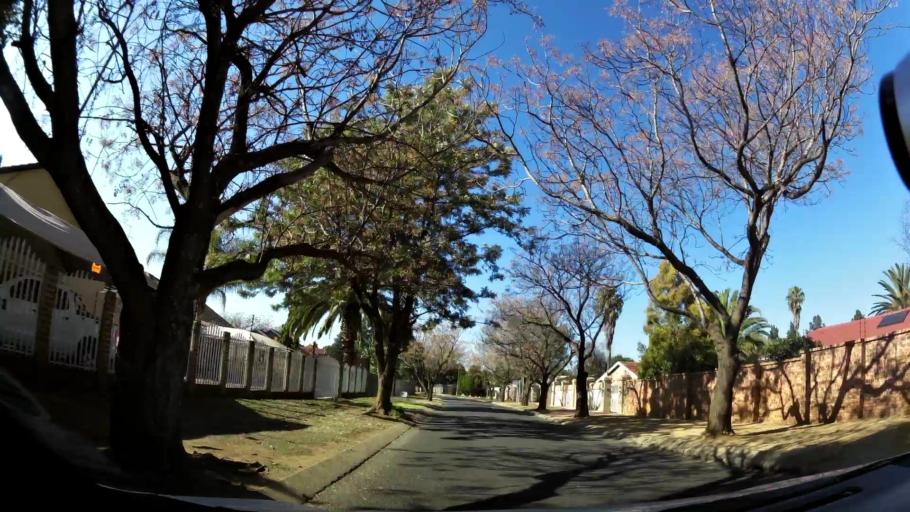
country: ZA
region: Gauteng
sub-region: Ekurhuleni Metropolitan Municipality
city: Germiston
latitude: -26.3303
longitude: 28.1037
